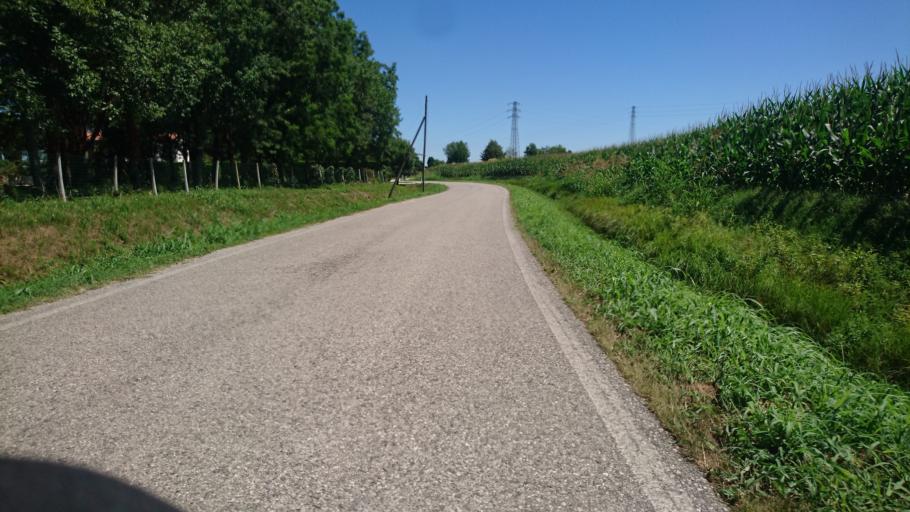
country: IT
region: Veneto
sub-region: Provincia di Padova
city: Campagnola
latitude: 45.2907
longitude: 12.0147
